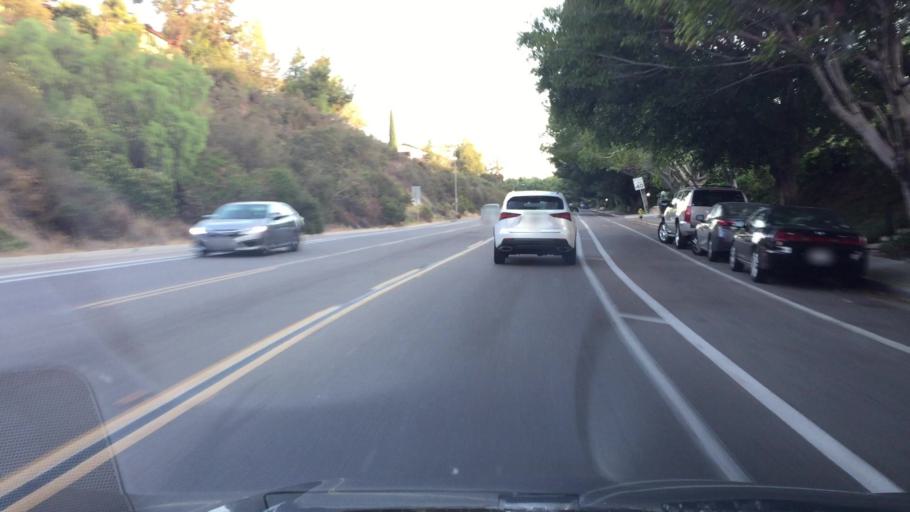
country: US
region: California
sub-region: San Diego County
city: Lemon Grove
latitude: 32.7661
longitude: -117.0836
